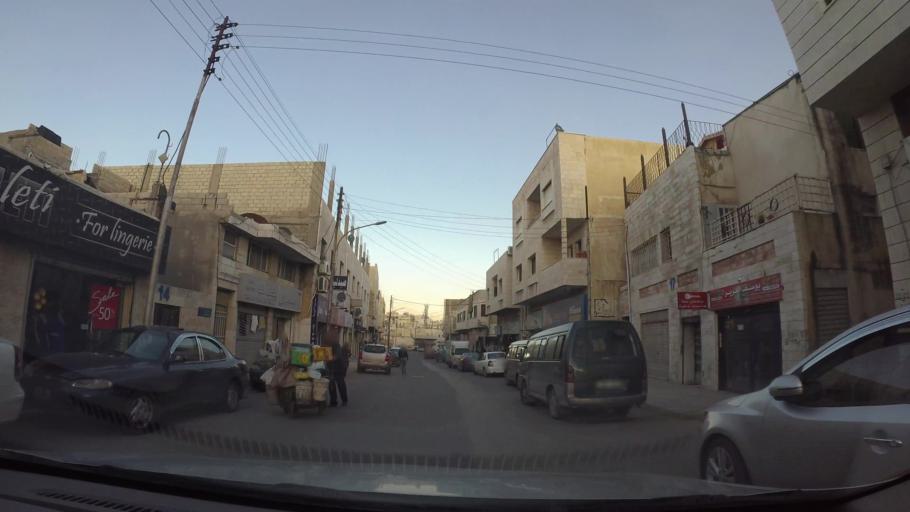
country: JO
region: Amman
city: Al Bunayyat ash Shamaliyah
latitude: 31.9059
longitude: 35.9100
